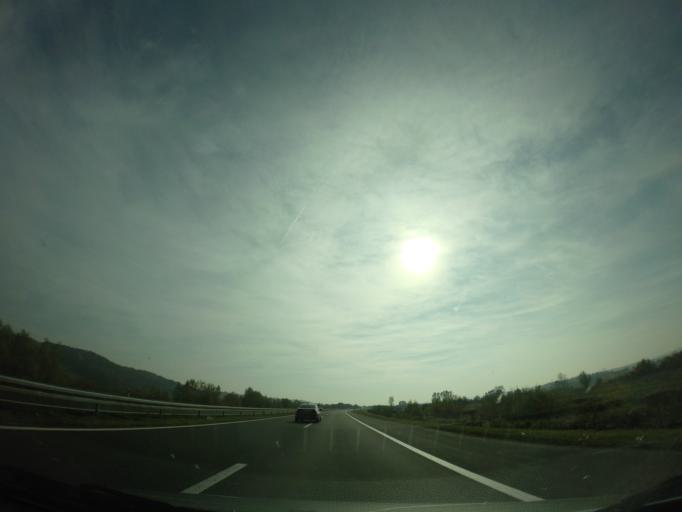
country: HR
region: Varazdinska
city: Remetinec
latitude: 46.0121
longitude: 16.2947
